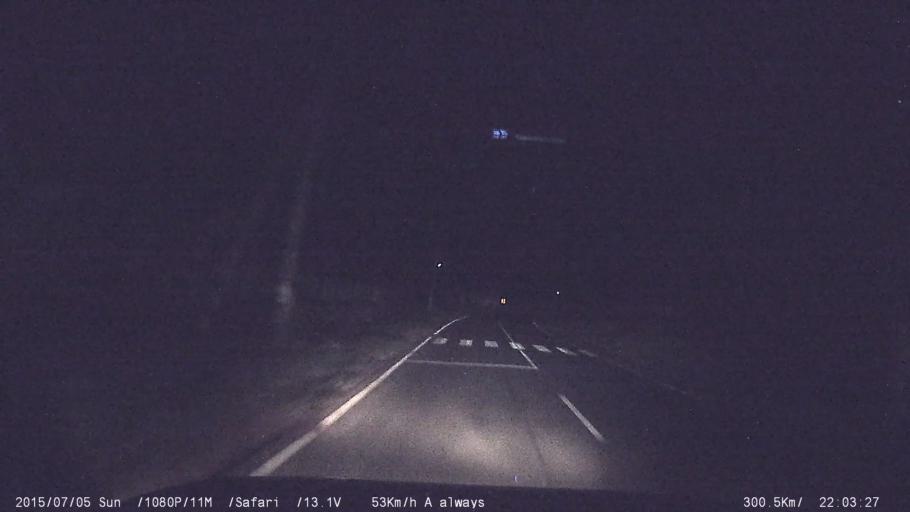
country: IN
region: Kerala
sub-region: Palakkad district
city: Mannarakkat
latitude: 10.9304
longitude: 76.5273
